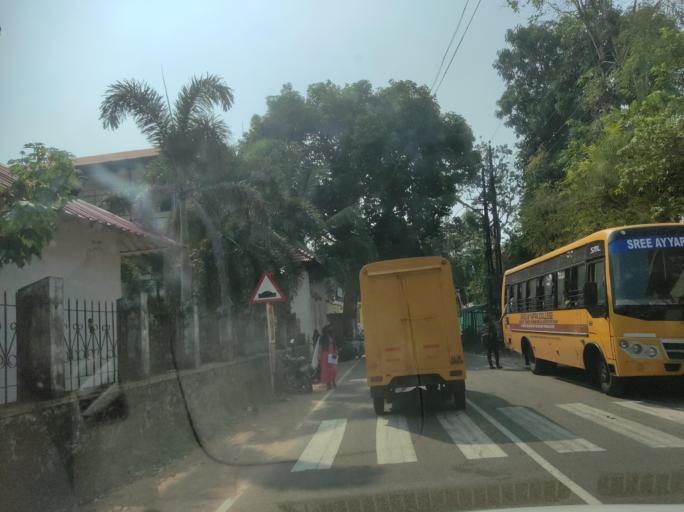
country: IN
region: Kerala
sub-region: Pattanamtitta
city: Tiruvalla
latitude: 9.3474
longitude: 76.5561
